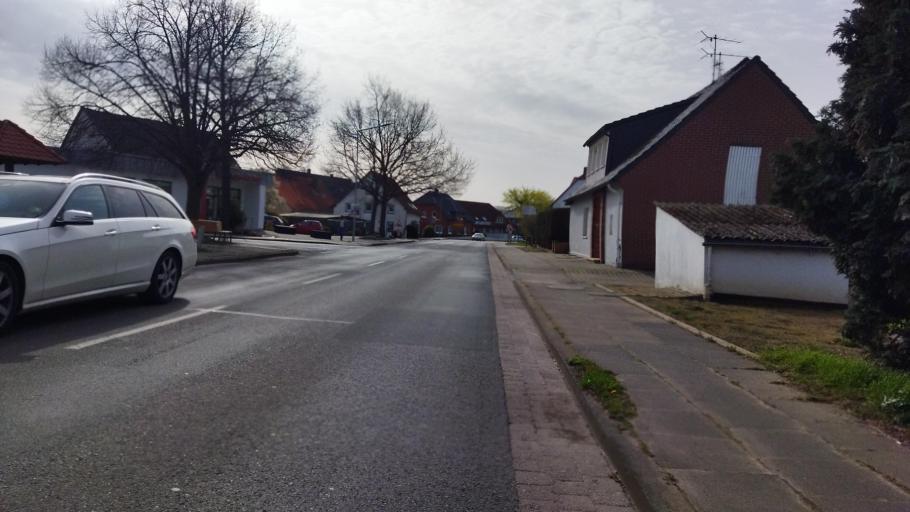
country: DE
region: Lower Saxony
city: Rinteln
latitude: 52.2019
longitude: 9.0131
